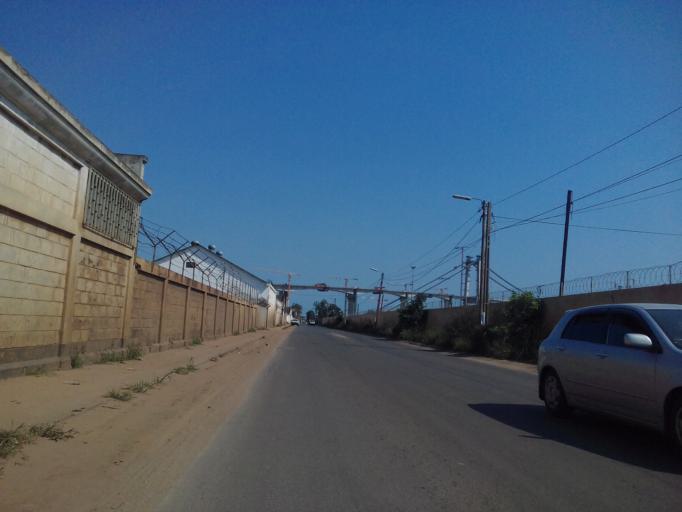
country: MZ
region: Maputo City
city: Maputo
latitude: -25.9595
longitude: 32.5550
